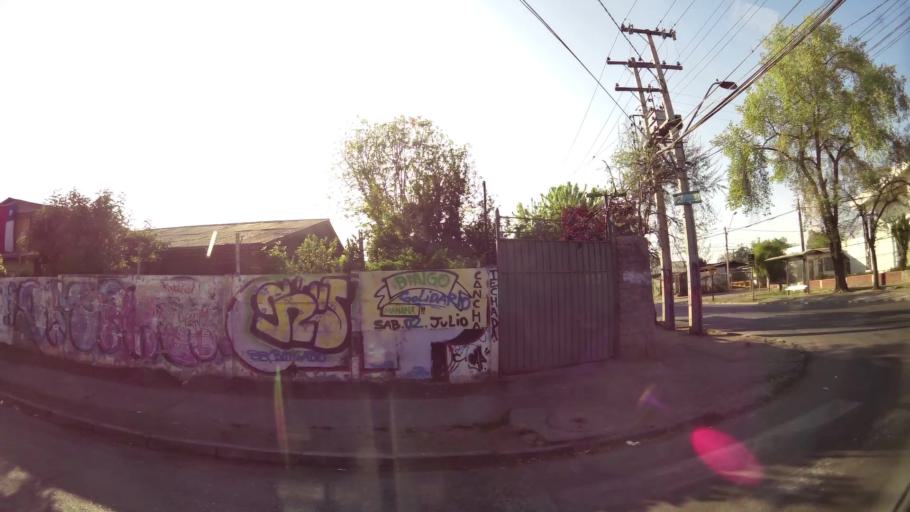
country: CL
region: Santiago Metropolitan
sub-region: Provincia de Santiago
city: Santiago
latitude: -33.3795
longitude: -70.6692
